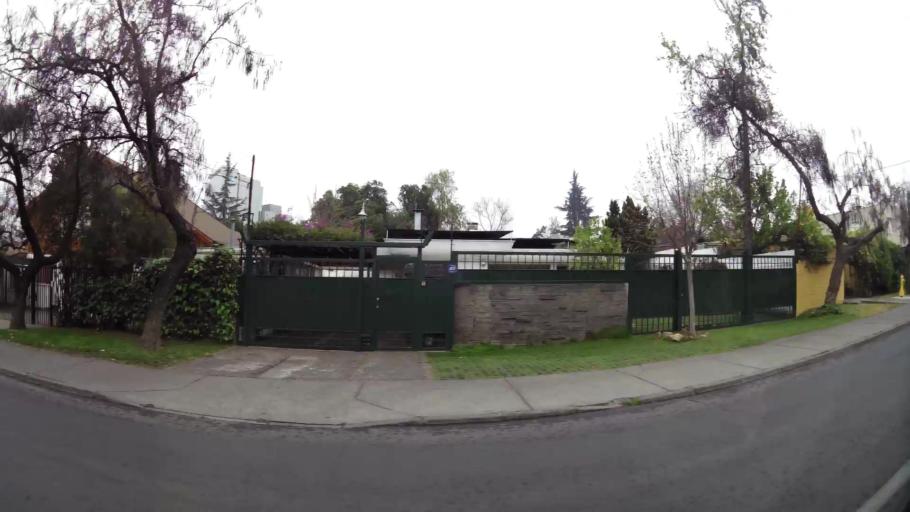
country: CL
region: Santiago Metropolitan
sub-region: Provincia de Santiago
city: Villa Presidente Frei, Nunoa, Santiago, Chile
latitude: -33.3941
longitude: -70.5708
